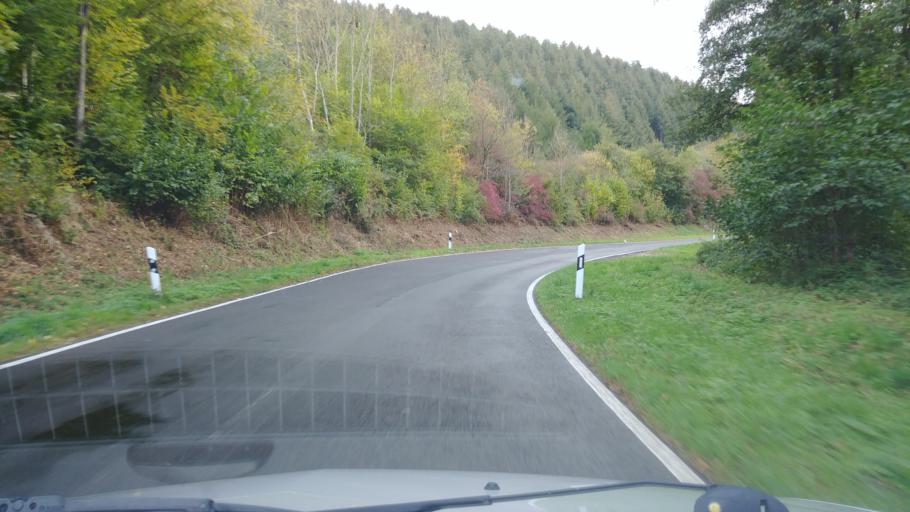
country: DE
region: Rheinland-Pfalz
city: Horath
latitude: 49.7944
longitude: 6.9836
